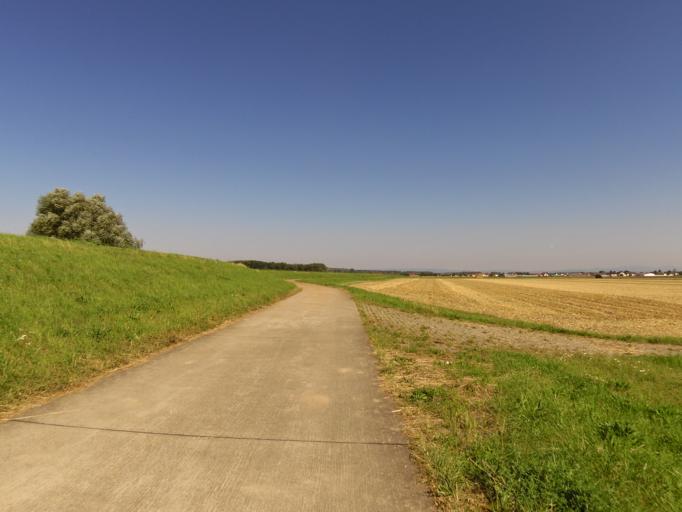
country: DE
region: Rheinland-Pfalz
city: Nierstein
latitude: 49.8746
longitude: 8.3674
